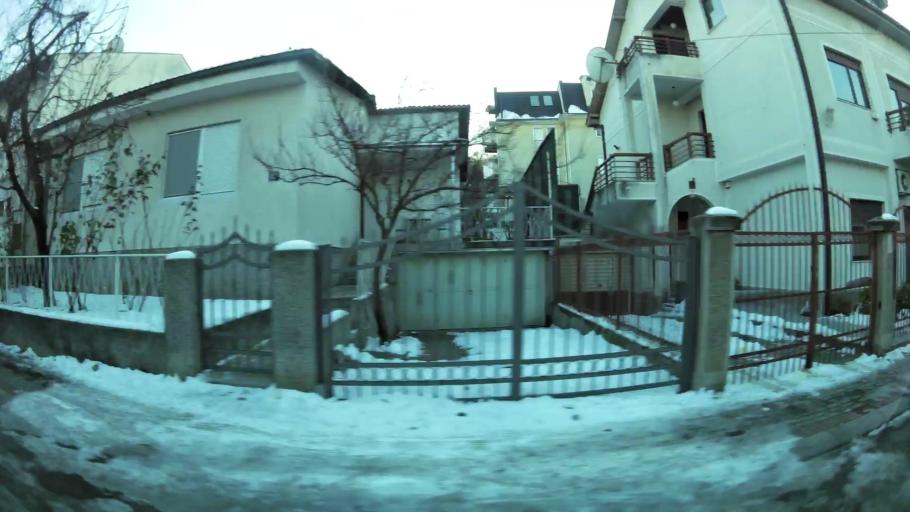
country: MK
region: Karpos
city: Skopje
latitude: 41.9927
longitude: 21.3985
